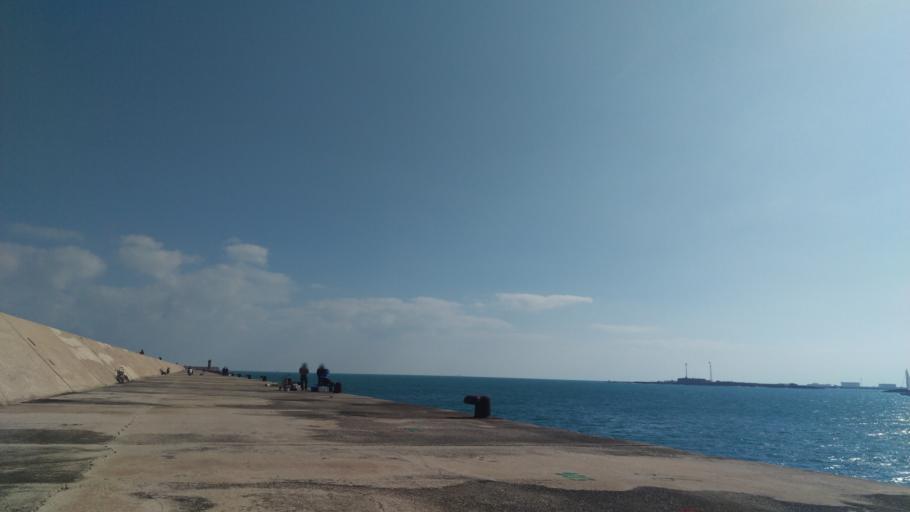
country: IT
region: Apulia
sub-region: Provincia di Brindisi
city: Materdomini
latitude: 40.6636
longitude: 17.9875
